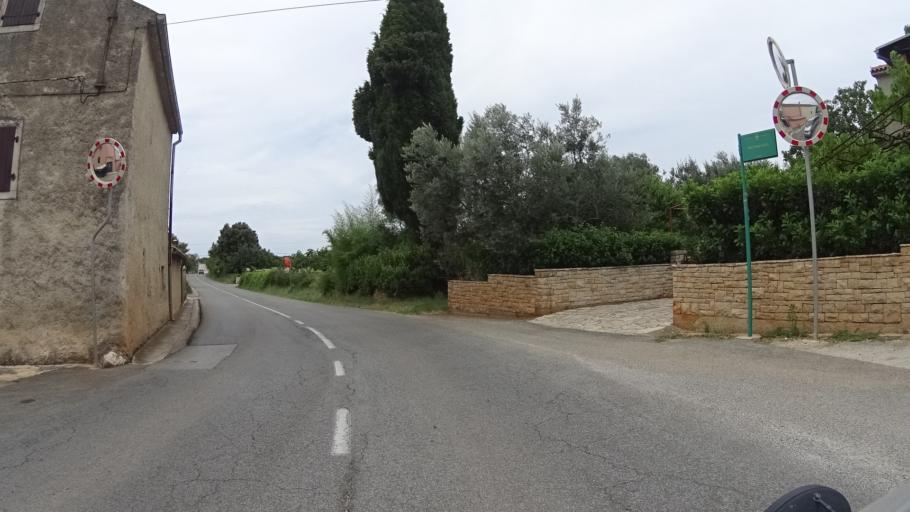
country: HR
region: Istarska
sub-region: Grad Pula
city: Pula
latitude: 44.8607
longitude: 13.8996
